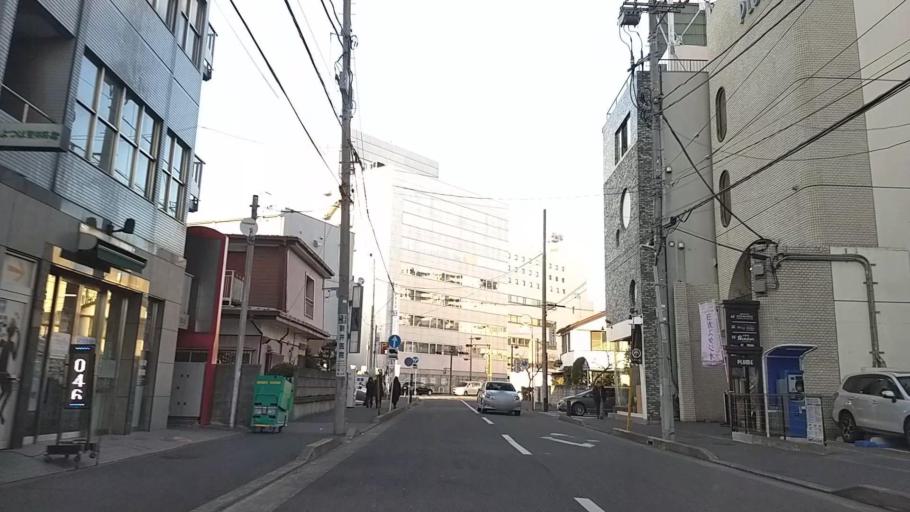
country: JP
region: Kanagawa
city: Atsugi
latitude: 35.4377
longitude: 139.3644
